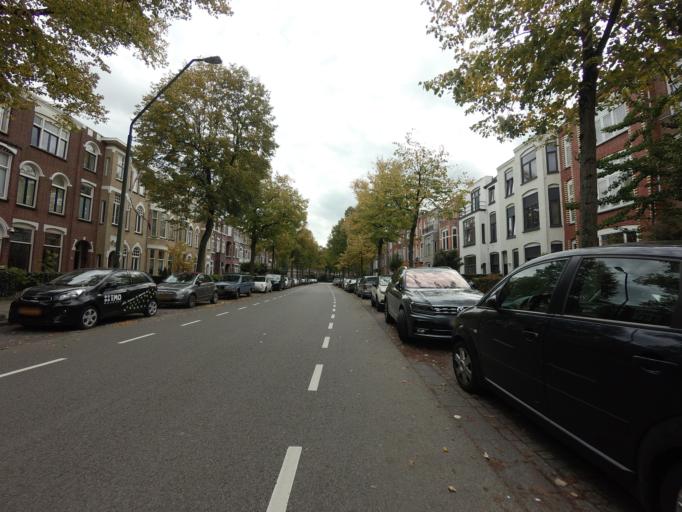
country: NL
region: North Brabant
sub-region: Gemeente Breda
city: Breda
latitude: 51.5695
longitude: 4.7767
